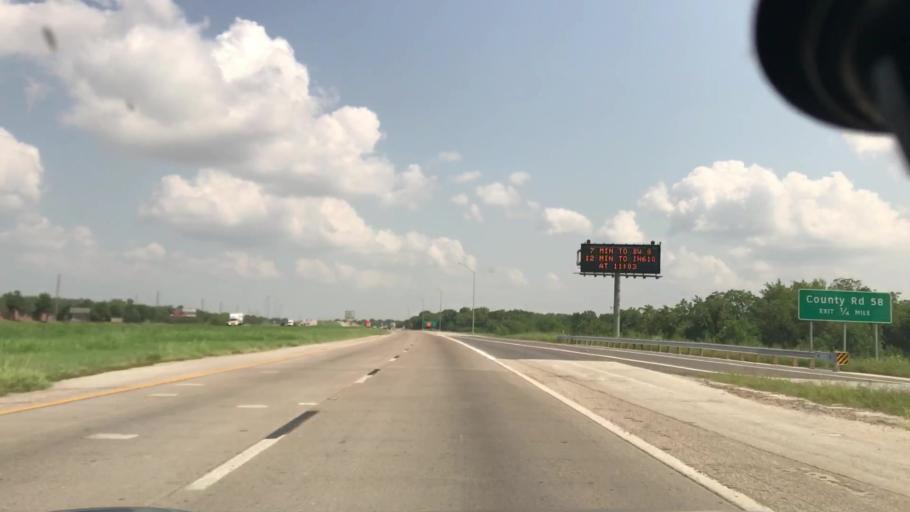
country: US
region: Texas
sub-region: Brazoria County
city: Iowa Colony
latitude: 29.5009
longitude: -95.3886
